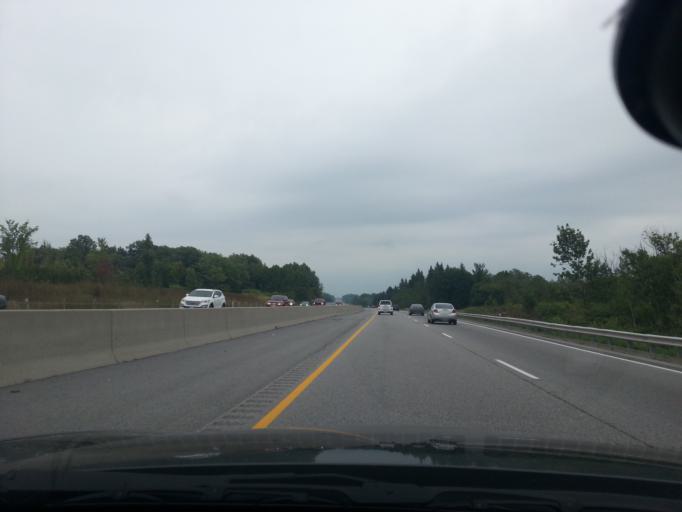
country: CA
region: Ontario
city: Gananoque
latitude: 44.3258
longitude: -76.2936
